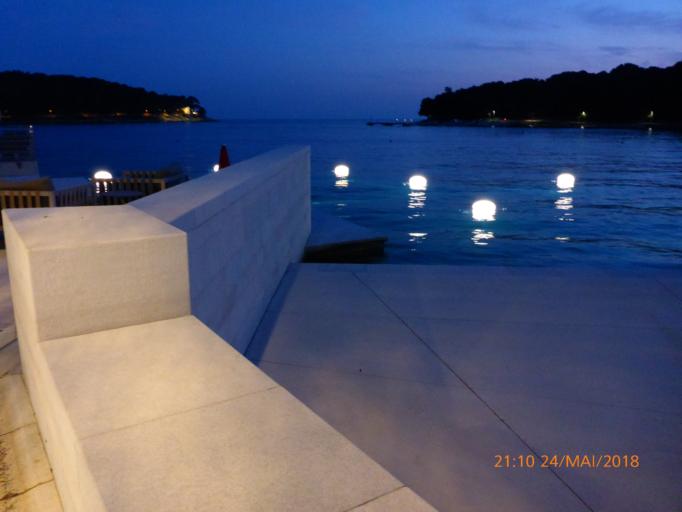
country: HR
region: Primorsko-Goranska
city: Mali Losinj
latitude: 44.5306
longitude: 14.4563
